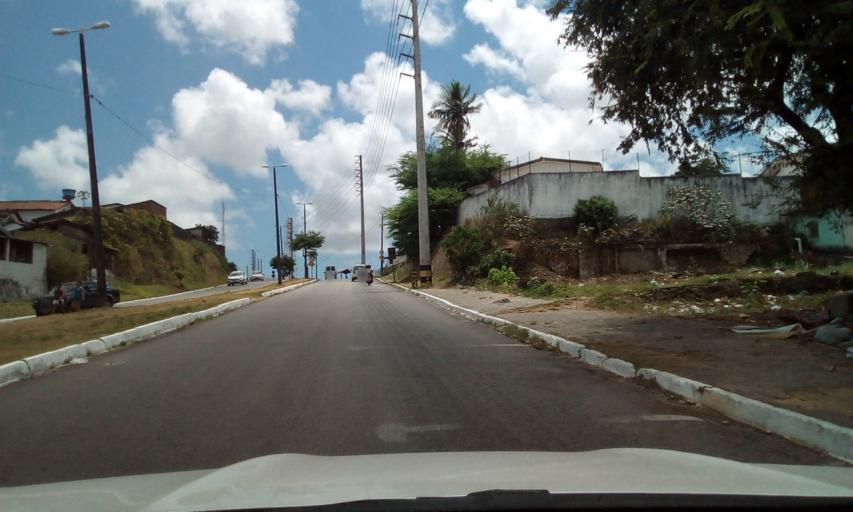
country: BR
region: Paraiba
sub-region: Joao Pessoa
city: Joao Pessoa
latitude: -7.1247
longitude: -34.8904
